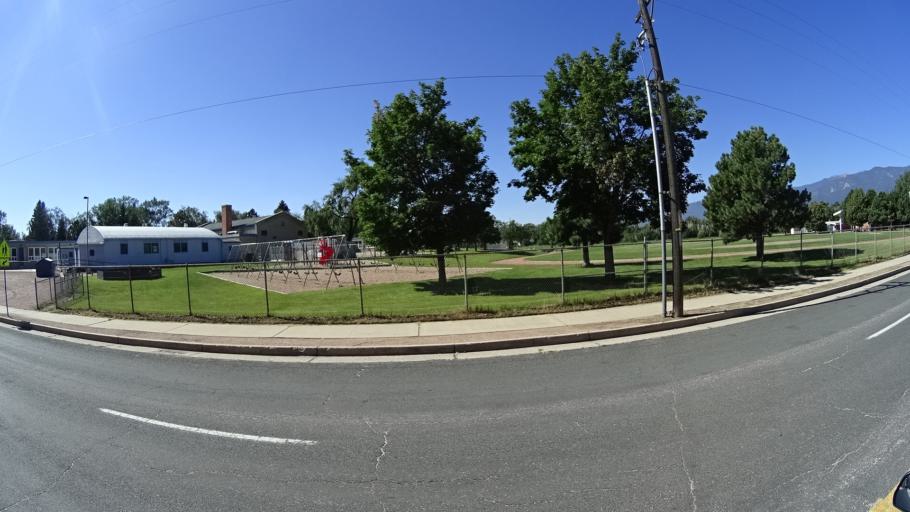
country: US
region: Colorado
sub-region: El Paso County
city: Colorado Springs
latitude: 38.8704
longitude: -104.7947
